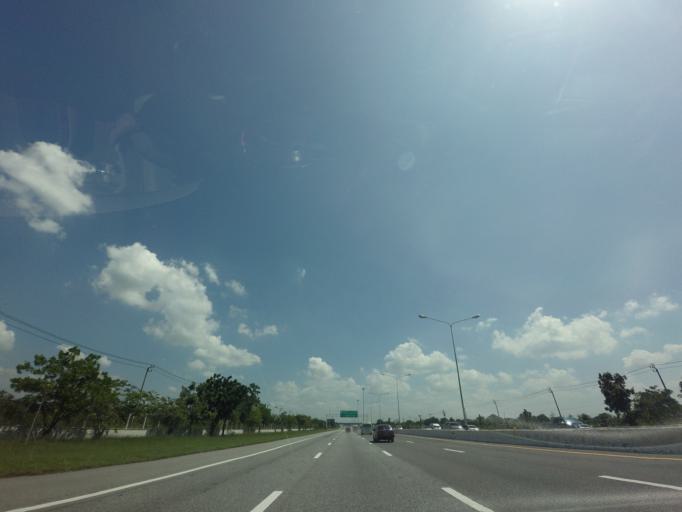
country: TH
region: Chachoengsao
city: Bang Pakong
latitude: 13.6124
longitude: 100.9338
